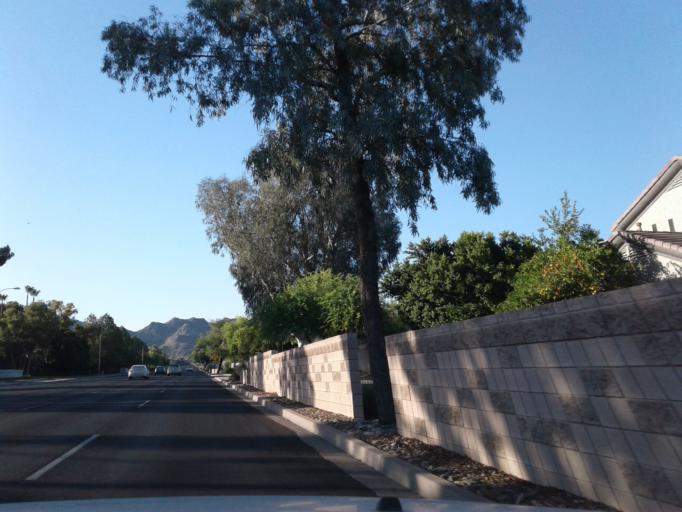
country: US
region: Arizona
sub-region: Maricopa County
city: Paradise Valley
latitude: 33.5133
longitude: -112.0129
